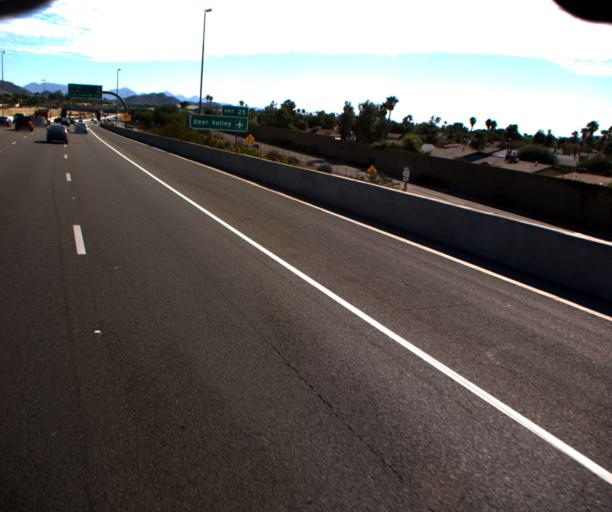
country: US
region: Arizona
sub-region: Maricopa County
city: Glendale
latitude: 33.6695
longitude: -112.0970
